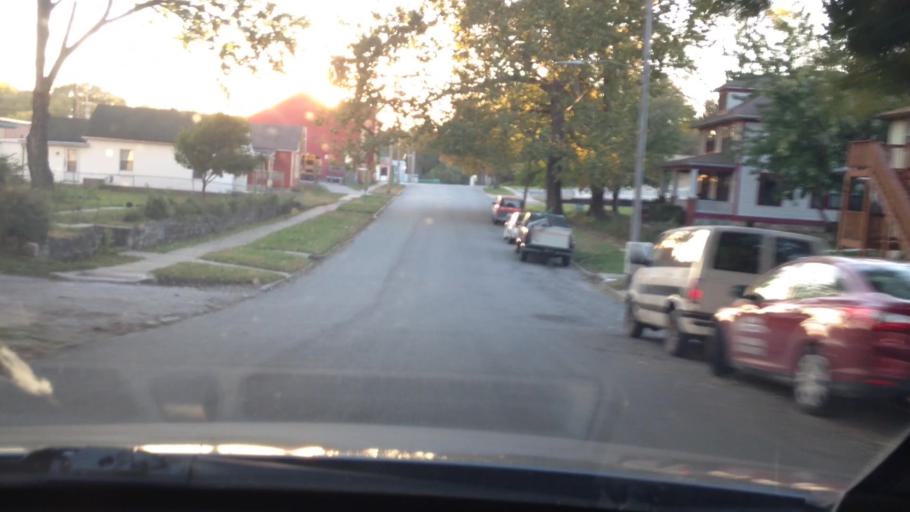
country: US
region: Kansas
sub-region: Leavenworth County
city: Leavenworth
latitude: 39.3192
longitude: -94.9199
